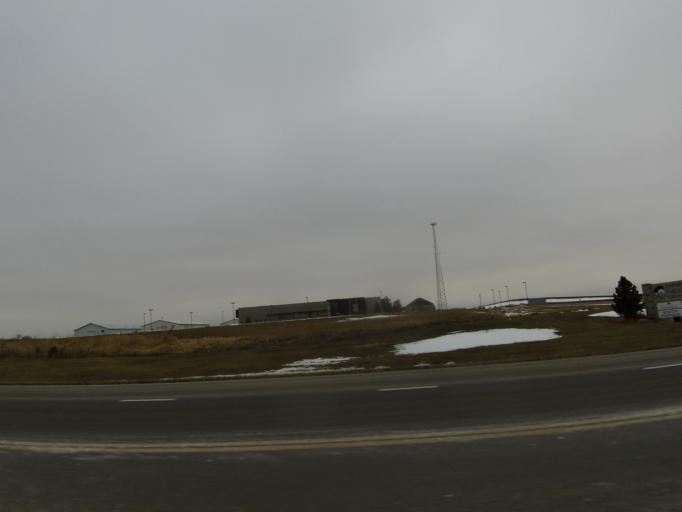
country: US
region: Minnesota
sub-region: Carver County
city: Cologne
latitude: 44.7677
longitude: -93.8130
